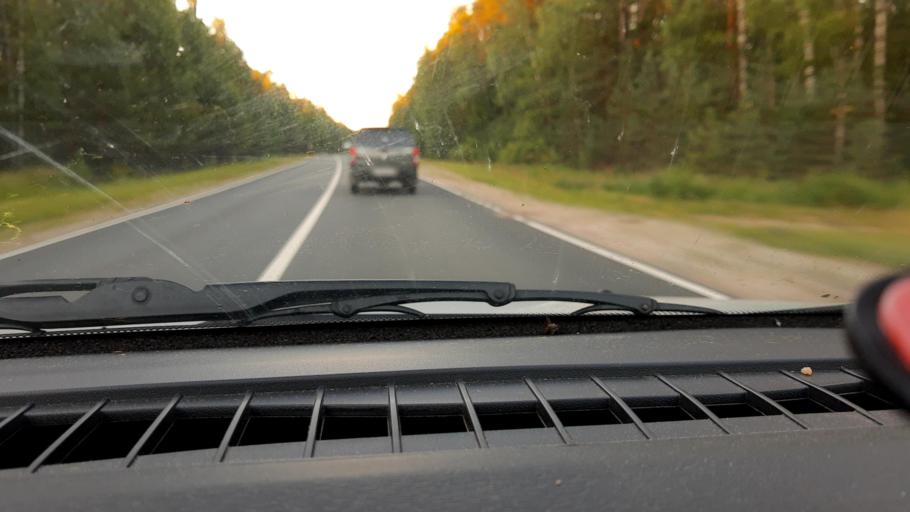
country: RU
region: Nizjnij Novgorod
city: Krasnyye Baki
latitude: 57.1651
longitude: 45.3070
